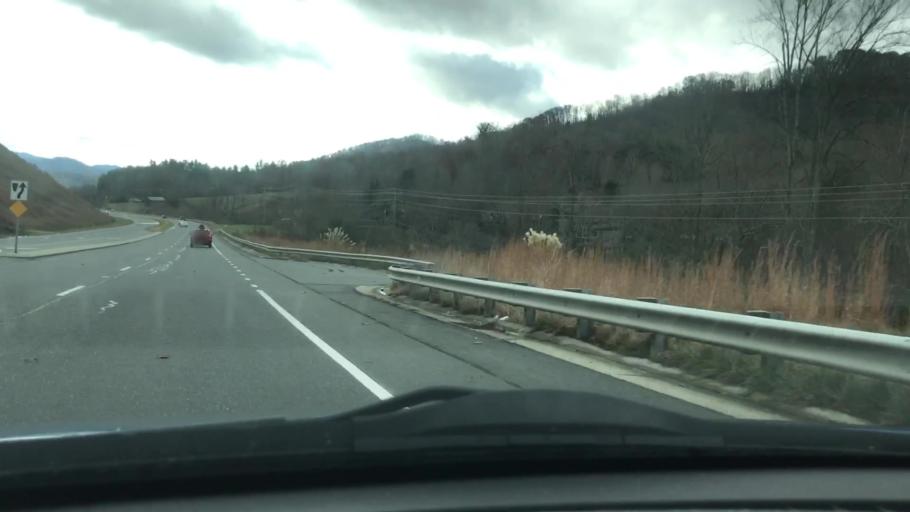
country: US
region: North Carolina
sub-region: Madison County
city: Mars Hill
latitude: 35.8920
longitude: -82.4751
